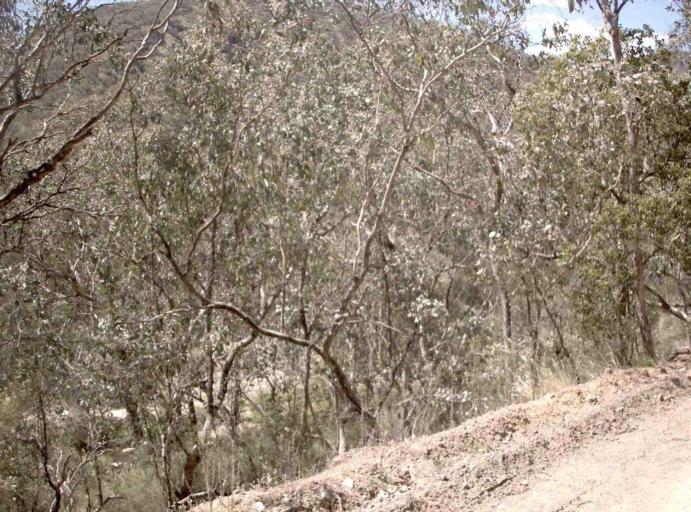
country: AU
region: New South Wales
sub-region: Snowy River
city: Jindabyne
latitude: -37.0678
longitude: 148.5021
